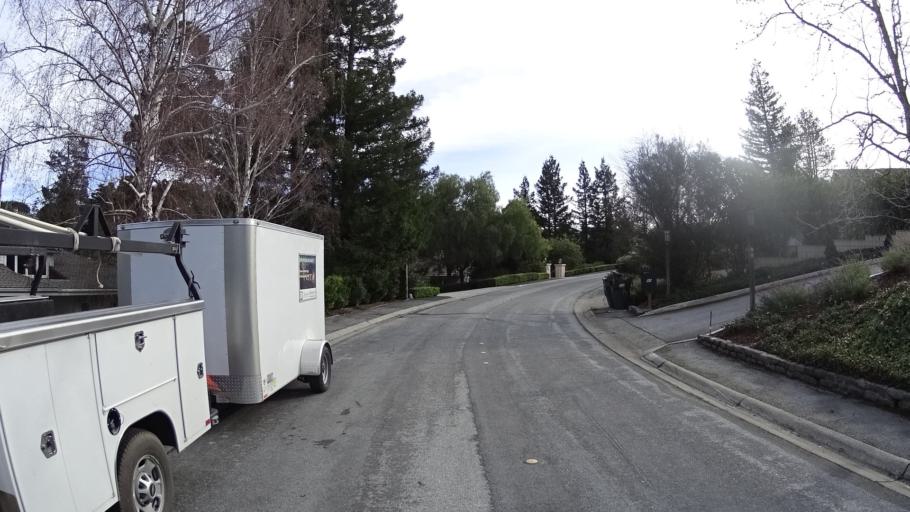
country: US
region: California
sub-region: San Mateo County
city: Burlingame
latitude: 37.5637
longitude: -122.3606
